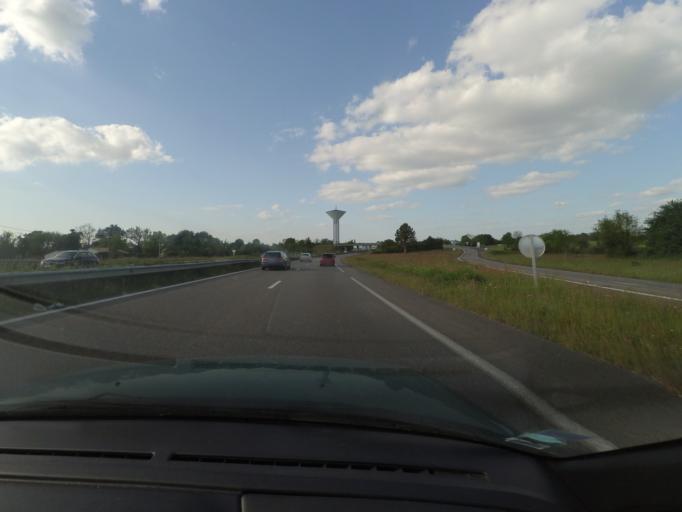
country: FR
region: Pays de la Loire
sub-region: Departement de la Vendee
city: Belleville-sur-Vie
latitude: 46.7686
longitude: -1.4307
